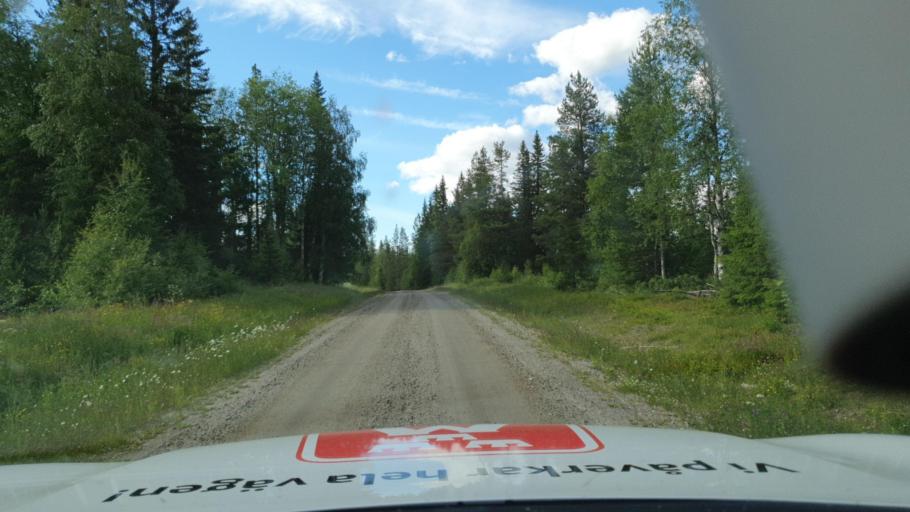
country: SE
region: Vaesterbotten
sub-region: Lycksele Kommun
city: Lycksele
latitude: 64.4582
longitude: 18.3080
